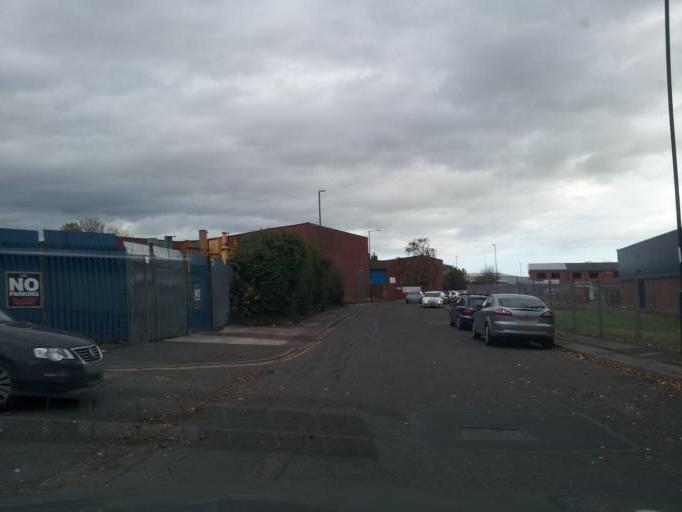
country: GB
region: England
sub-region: Nottinghamshire
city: West Bridgford
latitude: 52.9449
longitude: -1.1226
